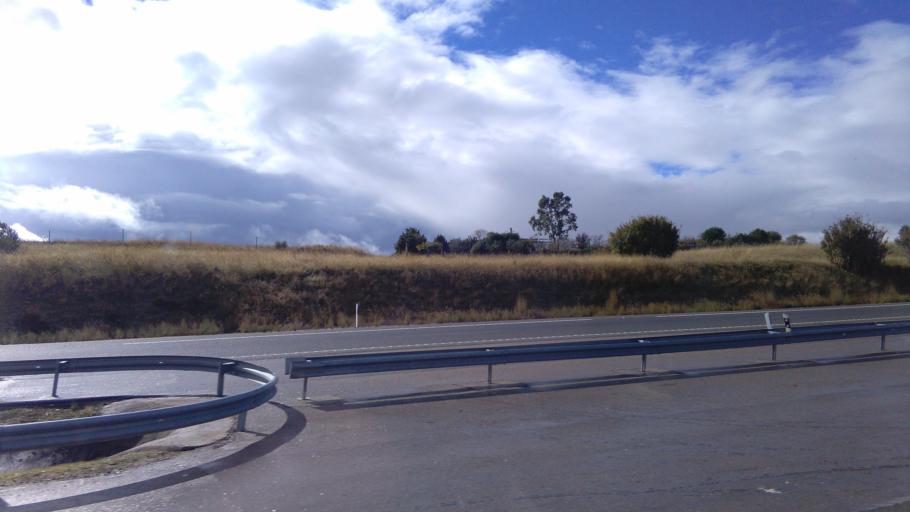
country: ES
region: Madrid
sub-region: Provincia de Madrid
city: Navalcarnero
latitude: 40.2655
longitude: -4.0229
